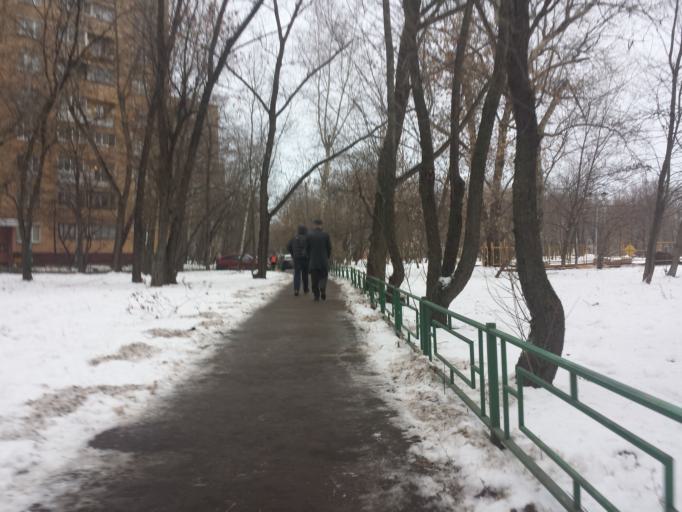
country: RU
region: Moskovskaya
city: Novogireyevo
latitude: 55.7487
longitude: 37.8269
